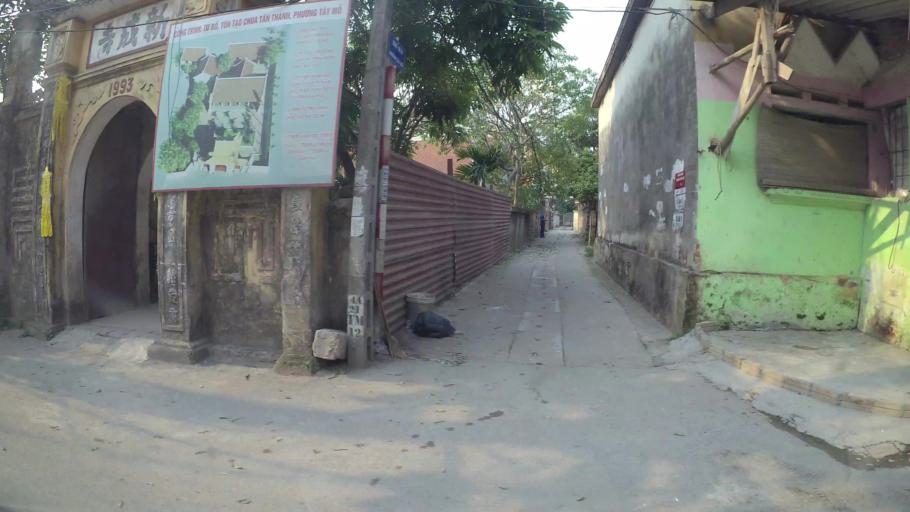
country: VN
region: Ha Noi
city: Cau Dien
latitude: 21.0016
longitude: 105.7489
